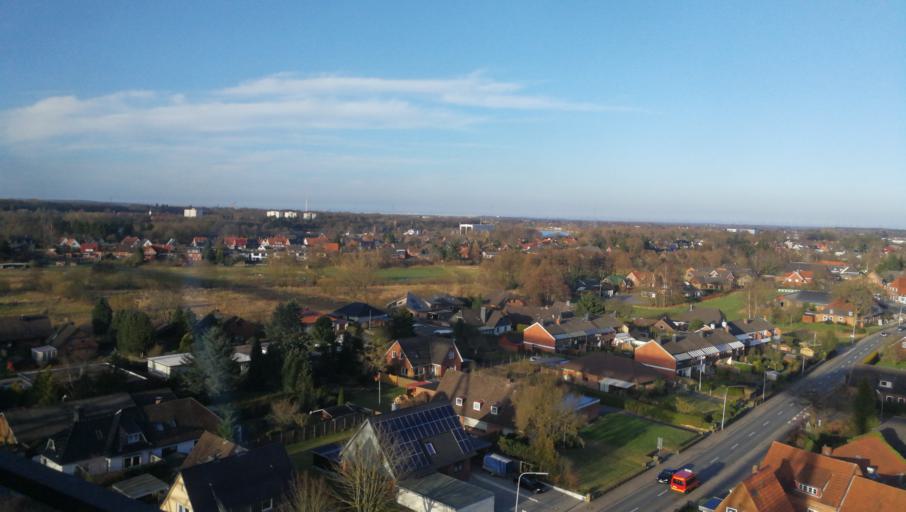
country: DE
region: Schleswig-Holstein
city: Osterronfeld
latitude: 54.2872
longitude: 9.6864
